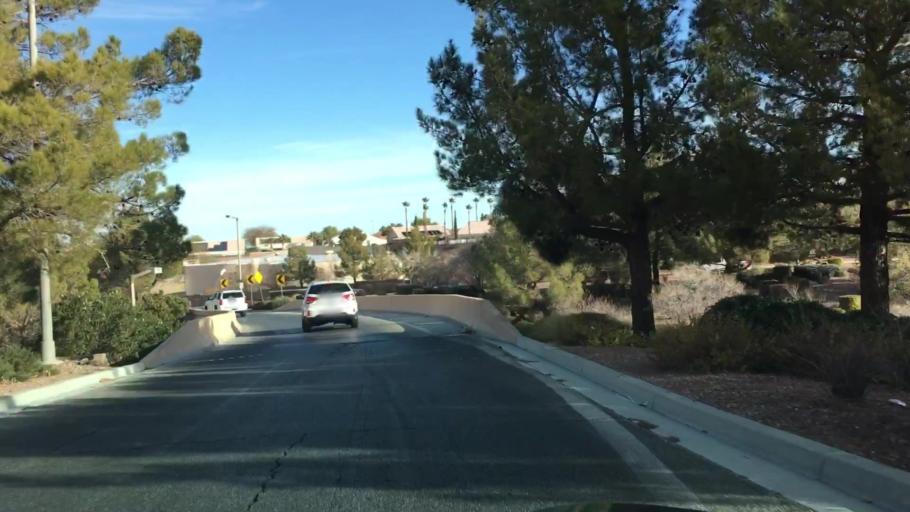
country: US
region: Nevada
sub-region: Clark County
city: Whitney
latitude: 35.9830
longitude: -115.1007
